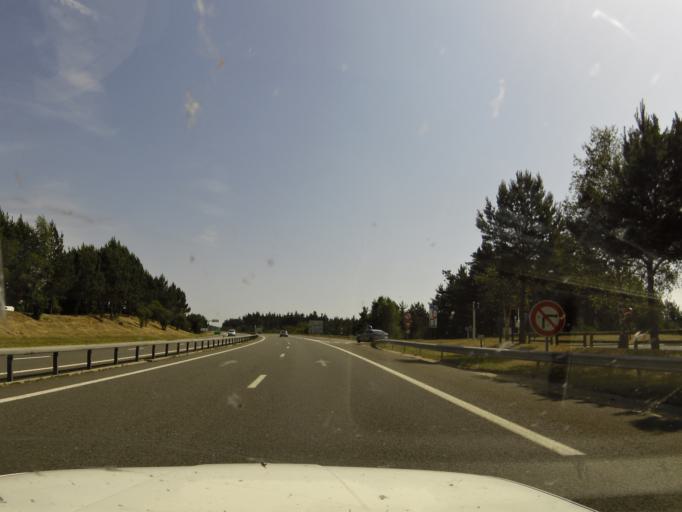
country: FR
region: Languedoc-Roussillon
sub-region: Departement de la Lozere
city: Aumont-Aubrac
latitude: 44.7453
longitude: 3.2882
